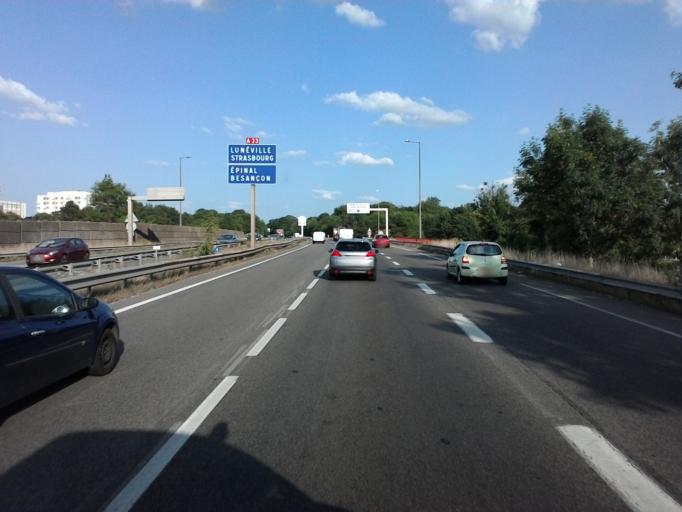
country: FR
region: Lorraine
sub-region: Departement de Meurthe-et-Moselle
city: Chavigny
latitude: 48.6468
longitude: 6.1392
